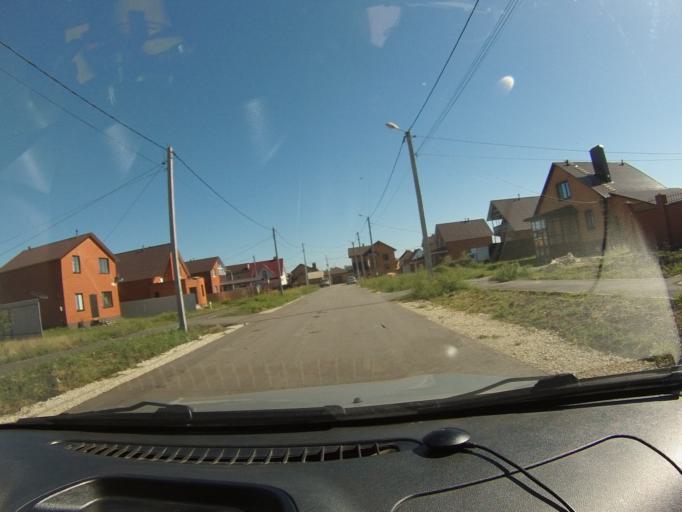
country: RU
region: Tambov
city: Tambov
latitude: 52.7704
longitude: 41.3741
